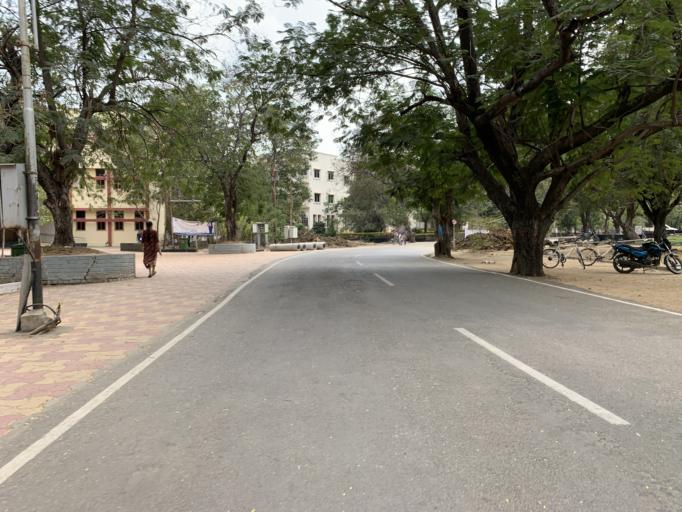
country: IN
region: Telangana
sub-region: Warangal
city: Warangal
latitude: 17.9846
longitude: 79.5318
